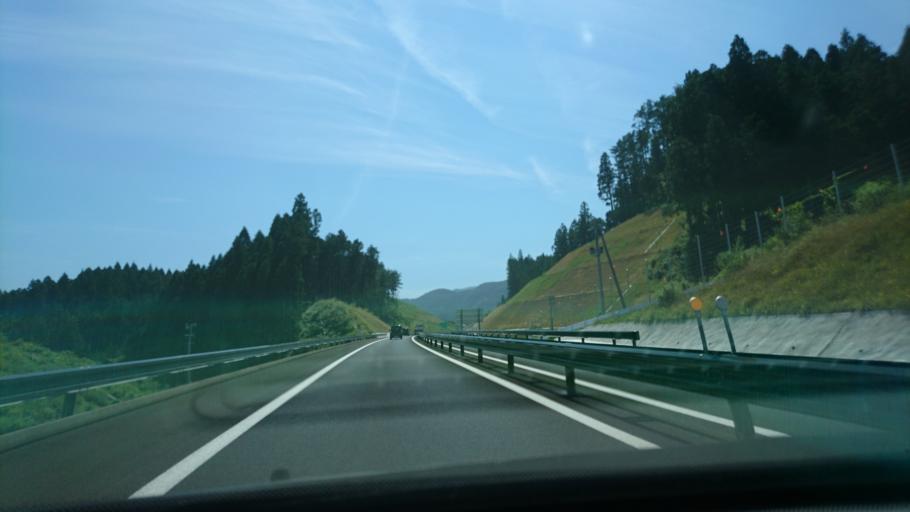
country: JP
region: Iwate
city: Ofunato
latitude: 38.9990
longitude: 141.6149
